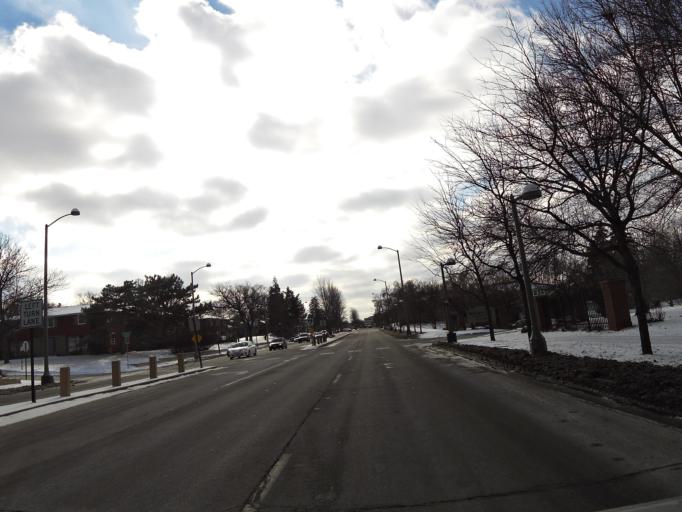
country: US
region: Minnesota
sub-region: Hennepin County
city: Saint Louis Park
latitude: 44.9395
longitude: -93.3305
